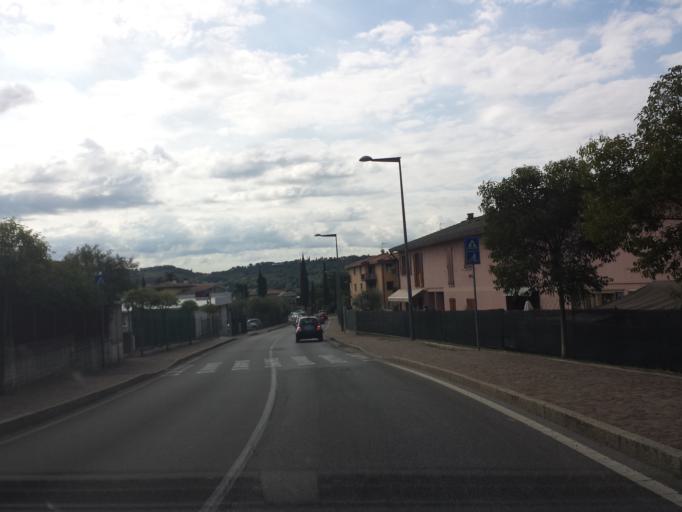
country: IT
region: Lombardy
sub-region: Provincia di Brescia
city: Salo
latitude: 45.6098
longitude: 10.5101
